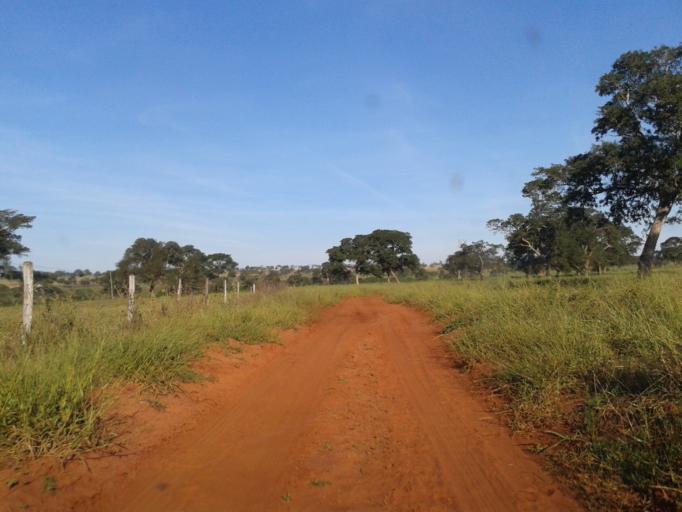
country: BR
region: Minas Gerais
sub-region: Santa Vitoria
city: Santa Vitoria
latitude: -19.0045
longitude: -50.3373
